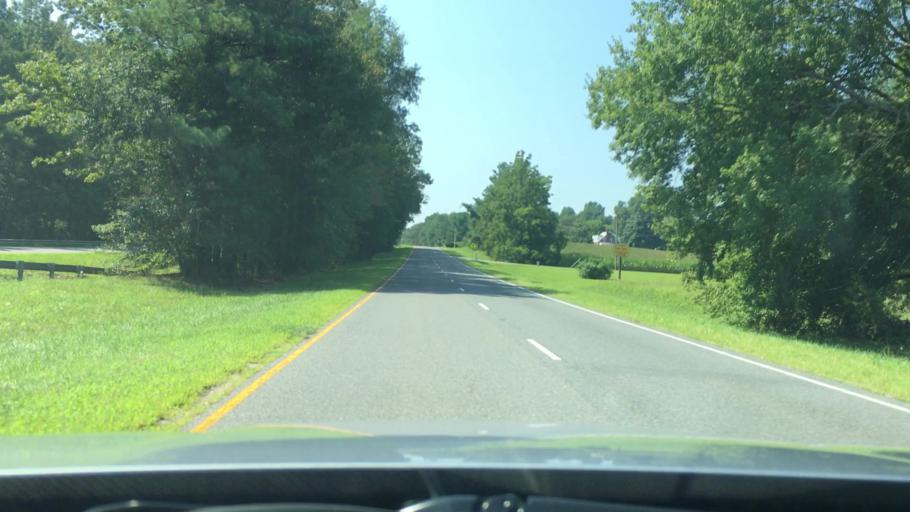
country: US
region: Virginia
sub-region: Caroline County
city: Bowling Green
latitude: 38.0057
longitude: -77.4146
